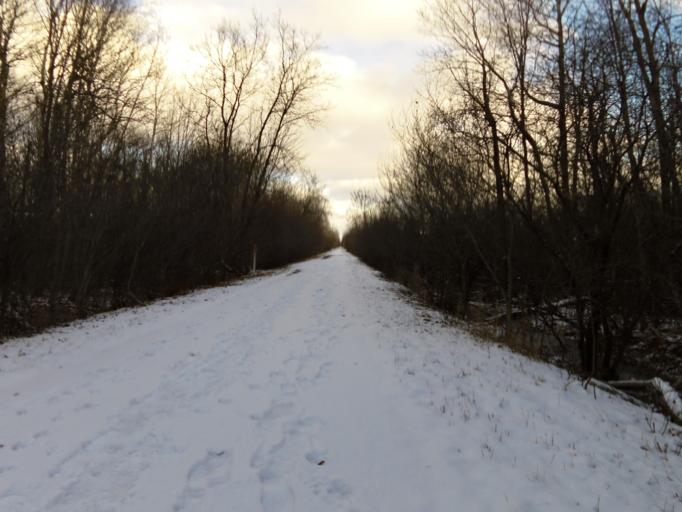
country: CA
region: Ontario
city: Ottawa
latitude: 45.4193
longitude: -75.5509
